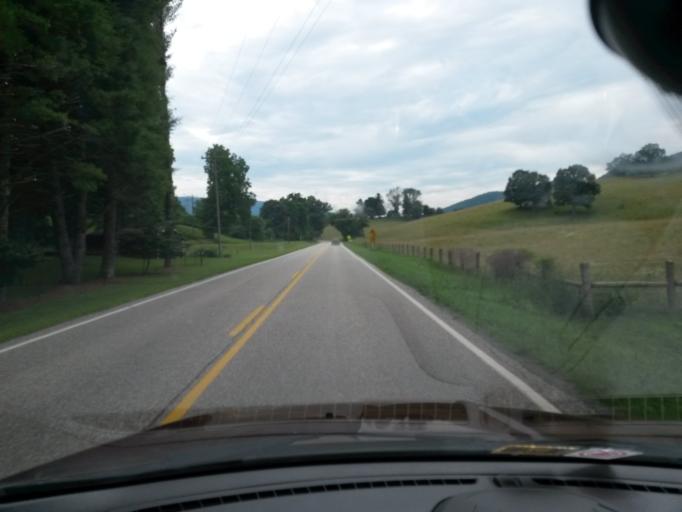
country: US
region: Virginia
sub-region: Alleghany County
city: Clifton Forge
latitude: 37.9017
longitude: -79.9017
